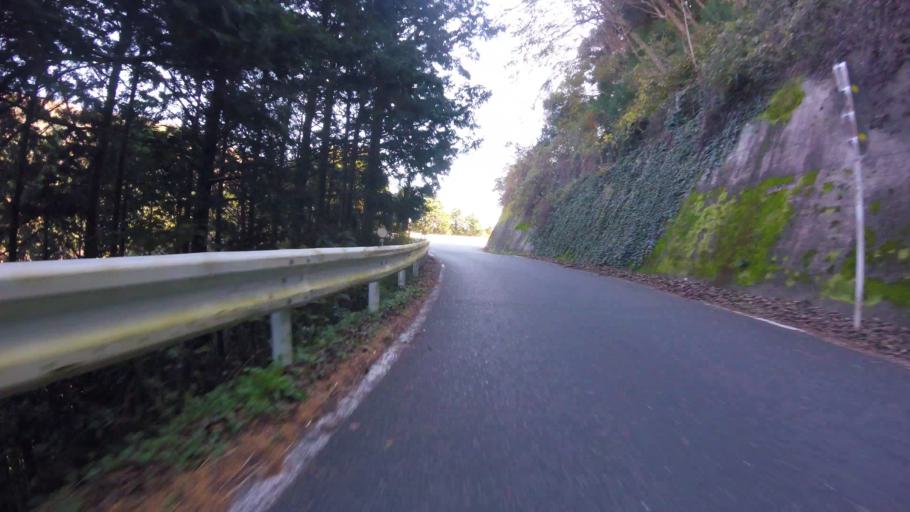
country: JP
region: Shizuoka
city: Shimoda
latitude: 34.7670
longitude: 138.9713
